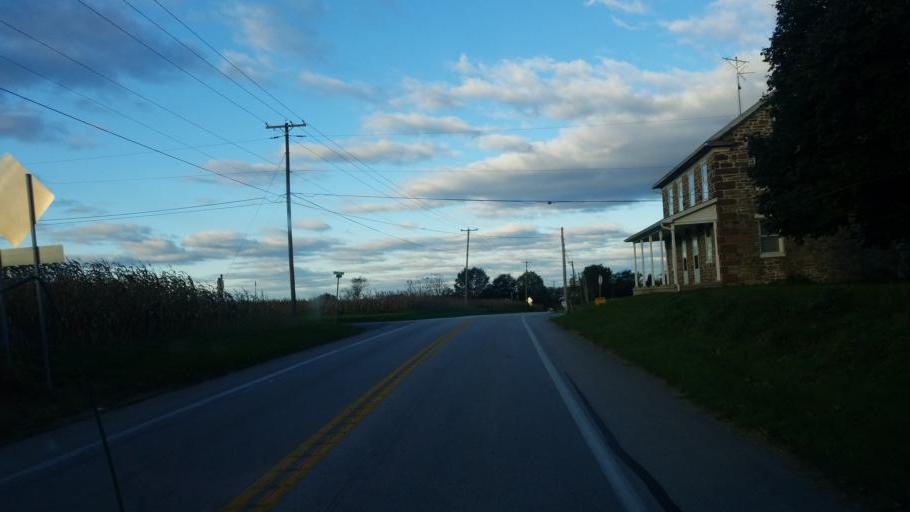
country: US
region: Pennsylvania
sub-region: Adams County
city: East Berlin
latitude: 39.9357
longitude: -76.9577
